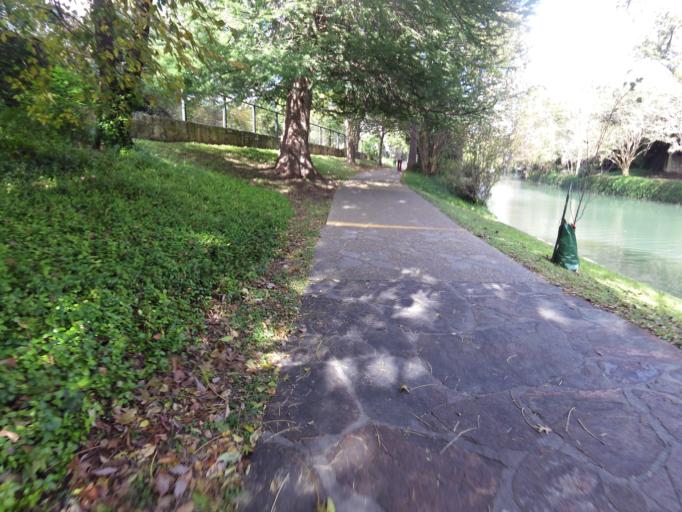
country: US
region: Texas
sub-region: Bexar County
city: San Antonio
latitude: 29.4142
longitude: -98.4952
